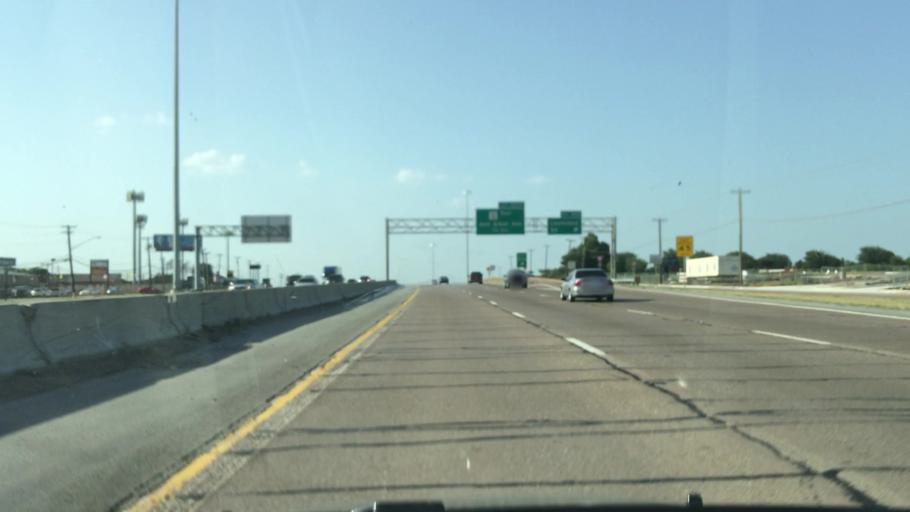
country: US
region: Texas
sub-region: Dallas County
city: DeSoto
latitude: 32.6701
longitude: -96.8225
